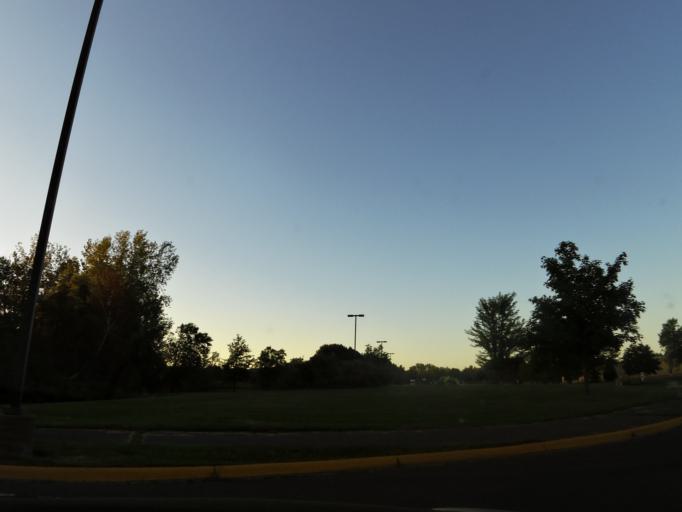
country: US
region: Minnesota
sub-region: Washington County
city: Oakdale
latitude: 44.9646
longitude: -92.9462
